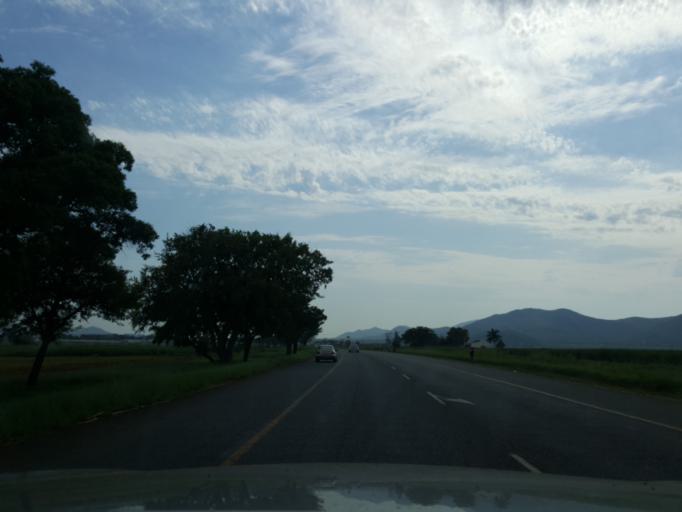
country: SZ
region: Hhohho
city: Ntfonjeni
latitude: -25.5051
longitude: 31.4955
